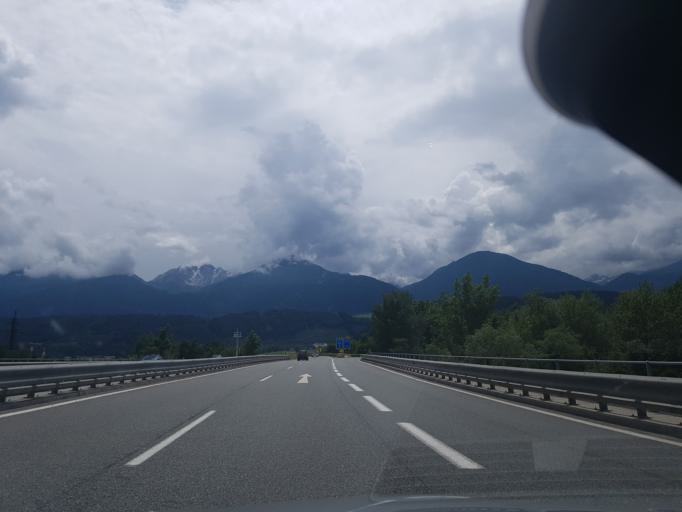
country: AT
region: Tyrol
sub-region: Politischer Bezirk Innsbruck Land
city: Unterperfuss
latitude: 47.2667
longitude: 11.2609
